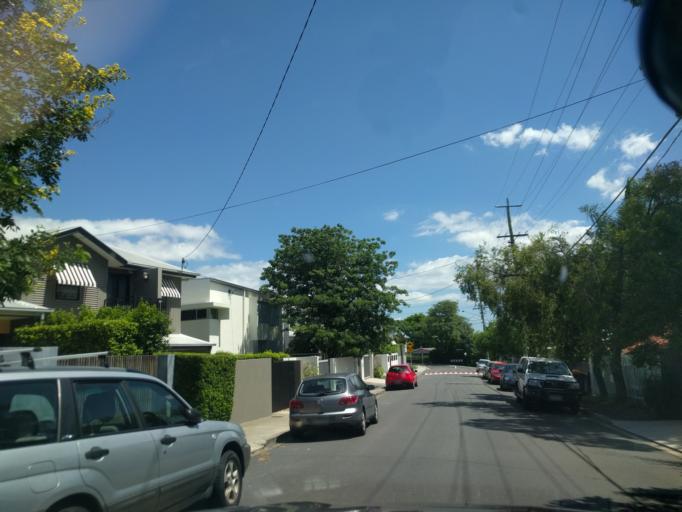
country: AU
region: Queensland
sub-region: Brisbane
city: Milton
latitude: -27.4573
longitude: 153.0073
